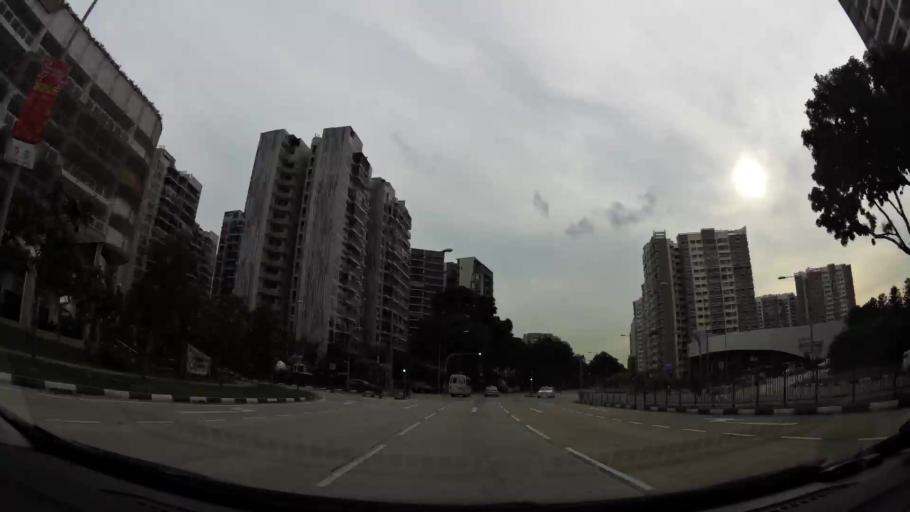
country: MY
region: Johor
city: Kampung Pasir Gudang Baru
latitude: 1.3777
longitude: 103.9033
